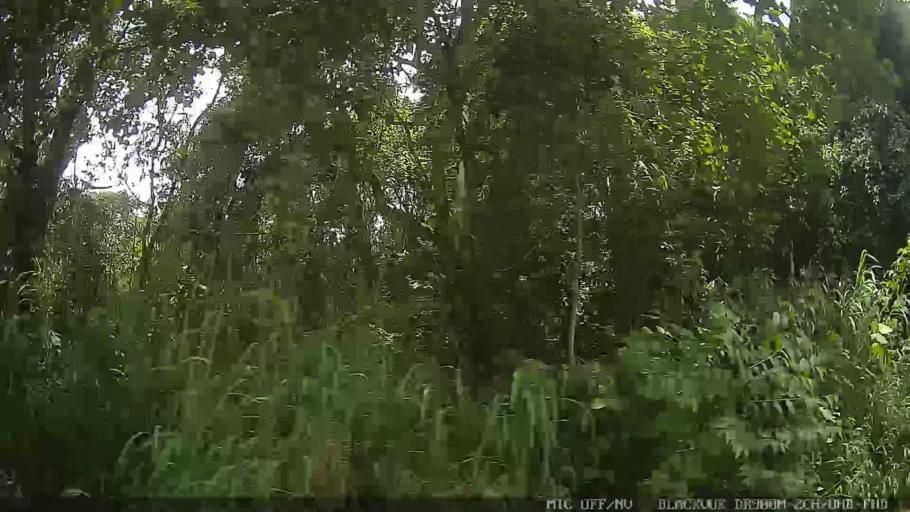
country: BR
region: Sao Paulo
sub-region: Santa Isabel
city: Santa Isabel
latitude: -23.3610
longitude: -46.2487
